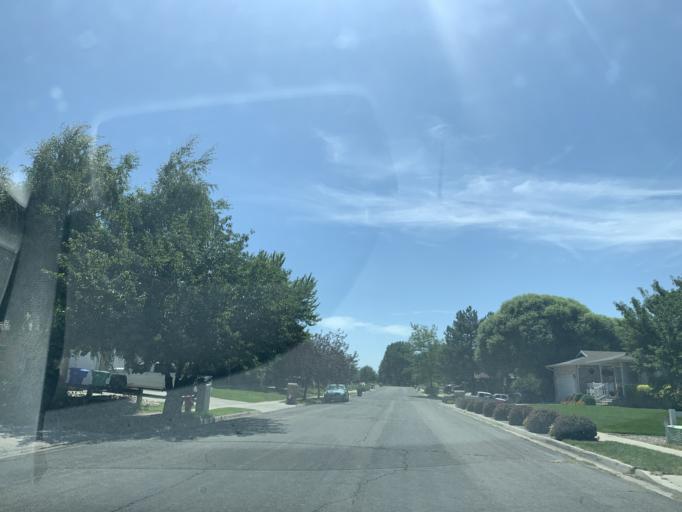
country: US
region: Utah
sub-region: Utah County
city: Lehi
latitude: 40.4084
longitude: -111.8273
